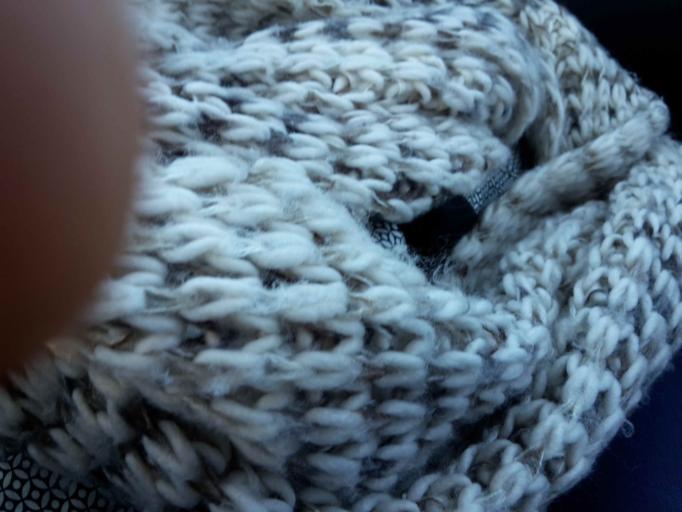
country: CH
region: Bern
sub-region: Emmental District
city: Durrenroth
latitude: 47.0981
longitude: 7.7763
